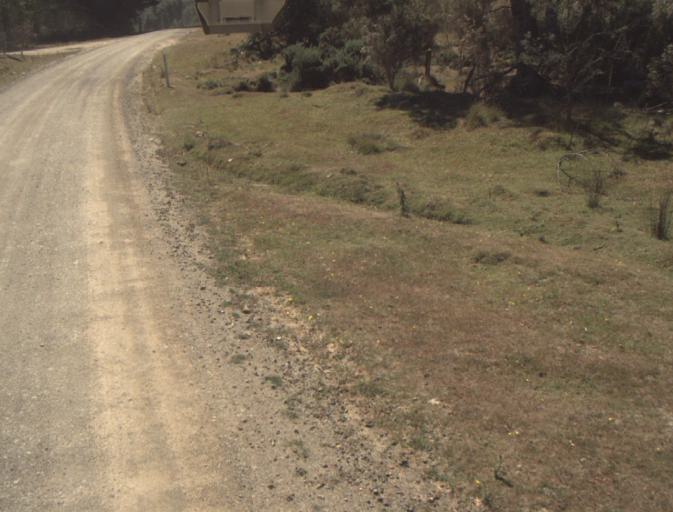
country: AU
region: Tasmania
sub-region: Dorset
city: Scottsdale
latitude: -41.3742
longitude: 147.4744
